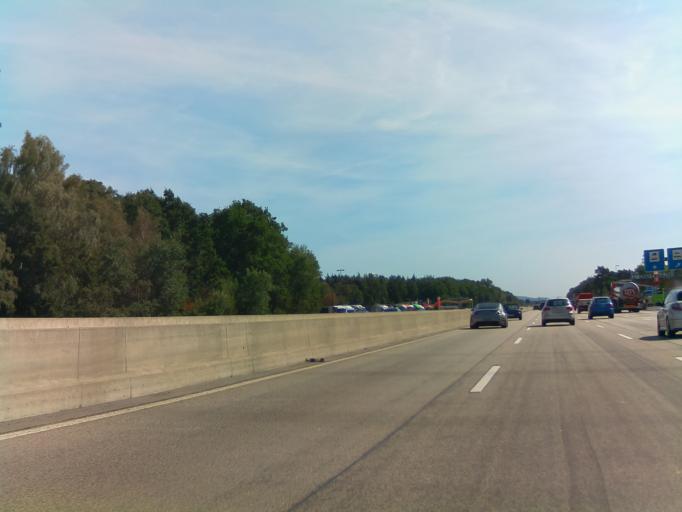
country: DE
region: Hesse
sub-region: Regierungsbezirk Darmstadt
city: Erzhausen
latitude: 49.9501
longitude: 8.6091
